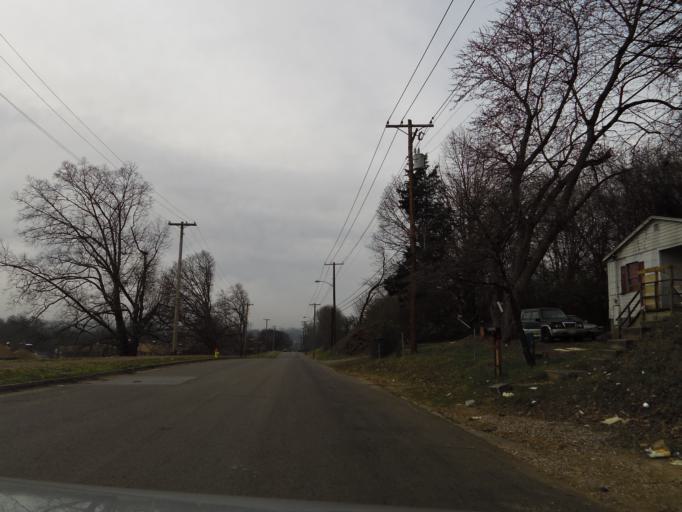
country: US
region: Tennessee
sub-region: Knox County
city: Knoxville
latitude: 35.9767
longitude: -83.9498
